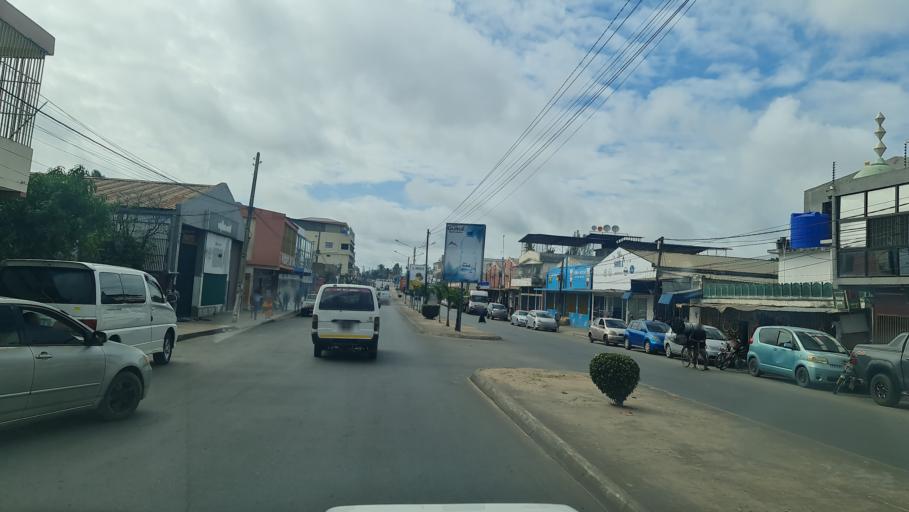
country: MZ
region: Nampula
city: Nampula
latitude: -15.1146
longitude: 39.2777
